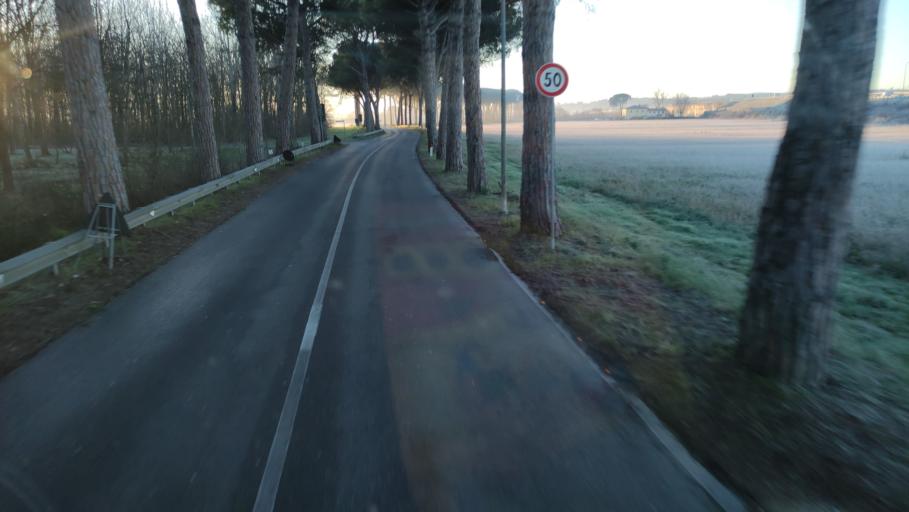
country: IT
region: Tuscany
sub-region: Province of Pisa
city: Ponte A Elsa
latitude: 43.6776
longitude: 10.9179
